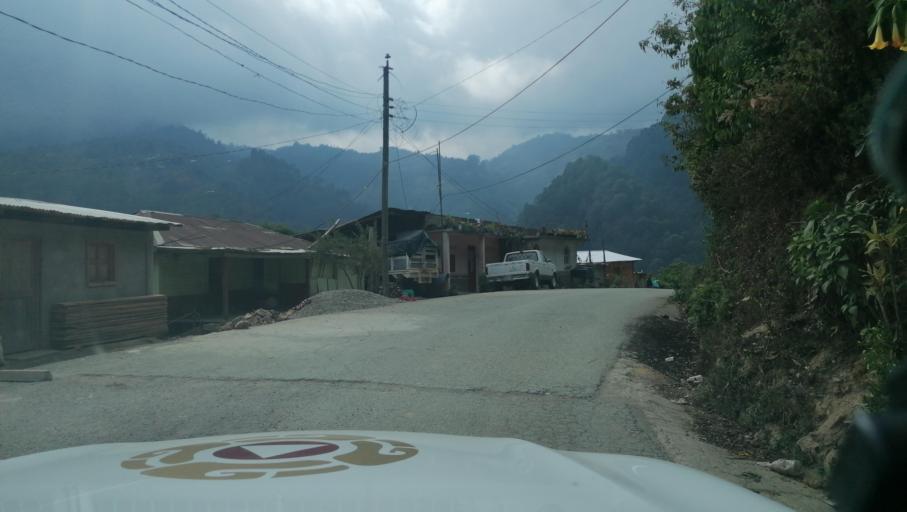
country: GT
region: San Marcos
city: Tacana
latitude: 15.2115
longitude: -92.1962
